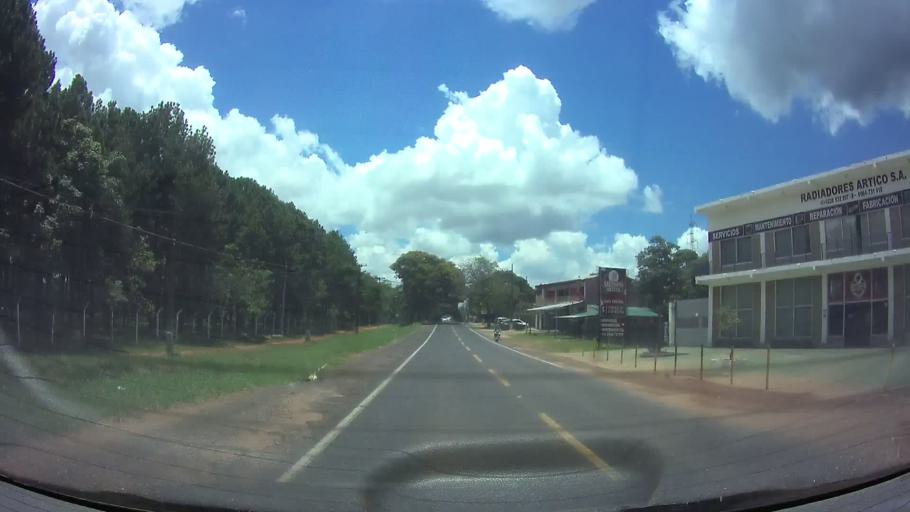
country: PY
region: Central
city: Capiata
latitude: -25.3595
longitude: -57.4260
